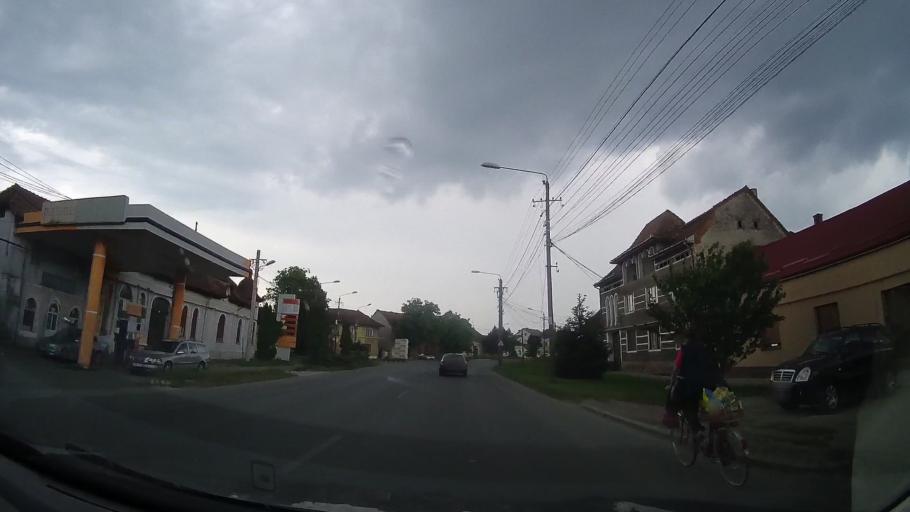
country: RO
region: Caras-Severin
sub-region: Municipiul Caransebes
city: Caransebes
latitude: 45.4058
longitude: 22.2238
